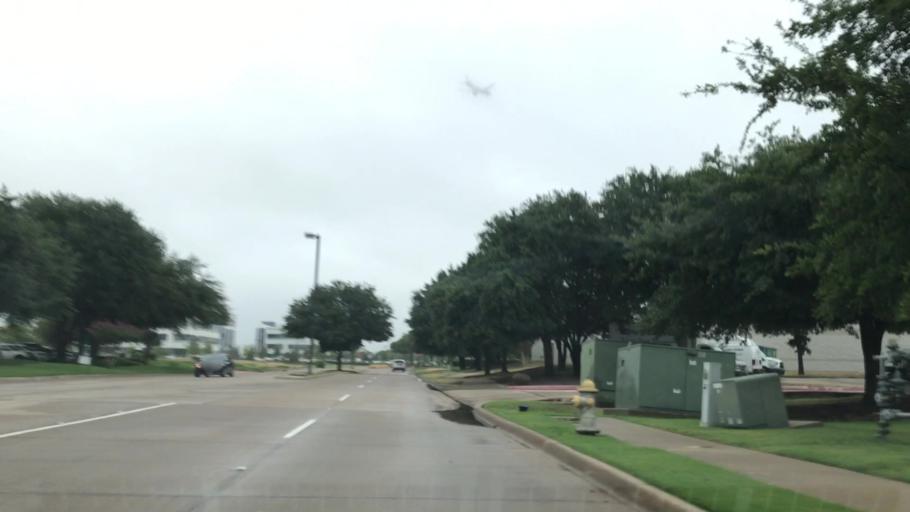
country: US
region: Texas
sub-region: Dallas County
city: Coppell
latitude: 32.9368
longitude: -97.0131
